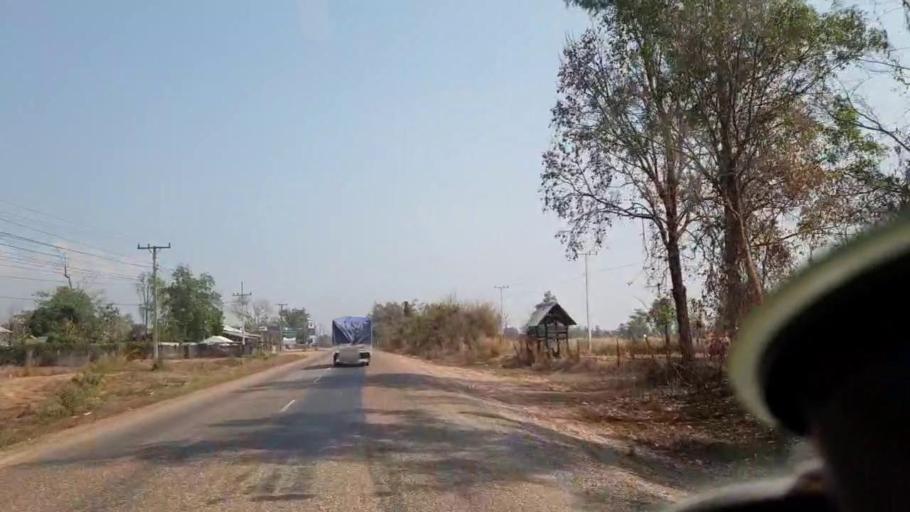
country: TH
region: Nong Khai
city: Phon Phisai
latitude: 18.0955
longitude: 103.0160
